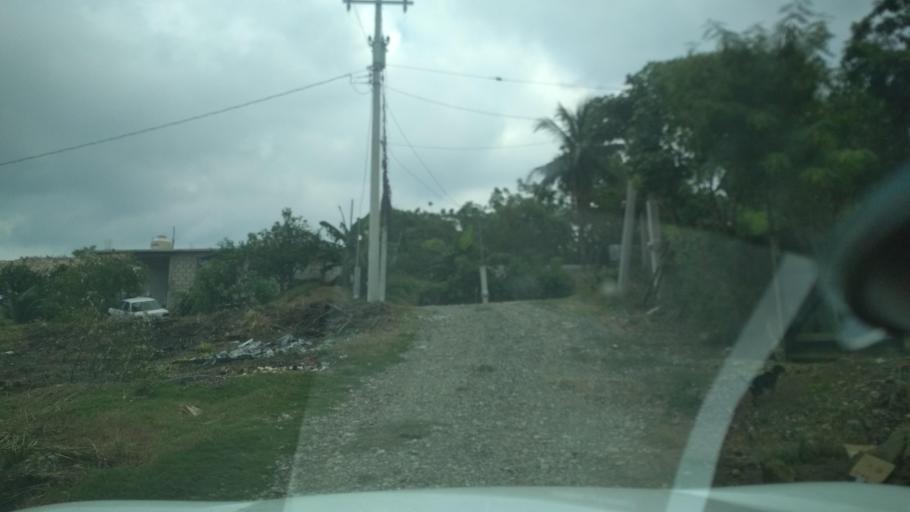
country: MX
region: Veracruz
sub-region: Poza Rica de Hidalgo
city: El Mollejon
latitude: 20.5152
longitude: -97.3807
